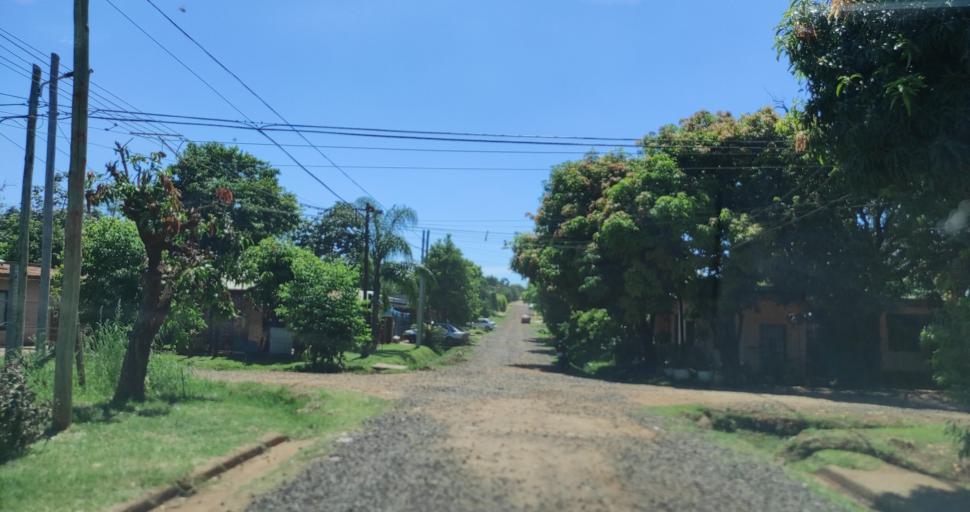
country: AR
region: Misiones
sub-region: Departamento de Capital
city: Posadas
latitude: -27.4084
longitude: -55.9160
